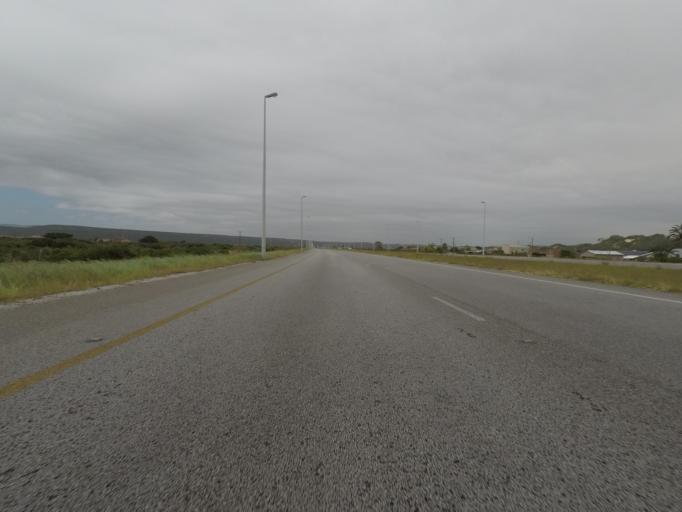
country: ZA
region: Eastern Cape
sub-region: Nelson Mandela Bay Metropolitan Municipality
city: Port Elizabeth
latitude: -33.7069
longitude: 25.8005
